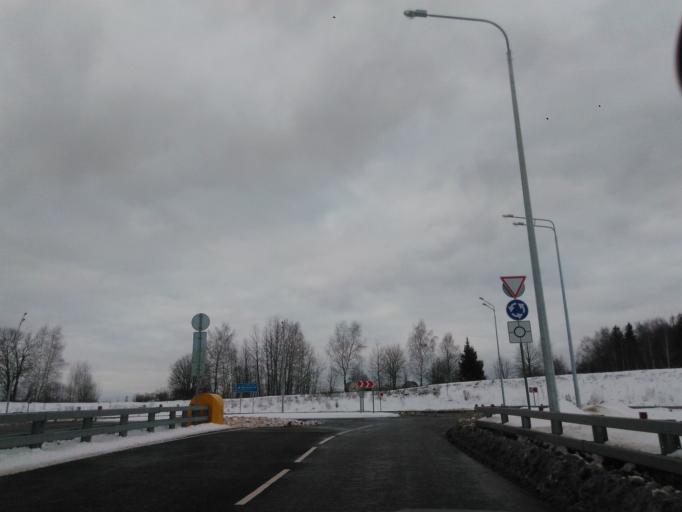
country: RU
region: Moskovskaya
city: Rzhavki
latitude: 56.0033
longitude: 37.2535
